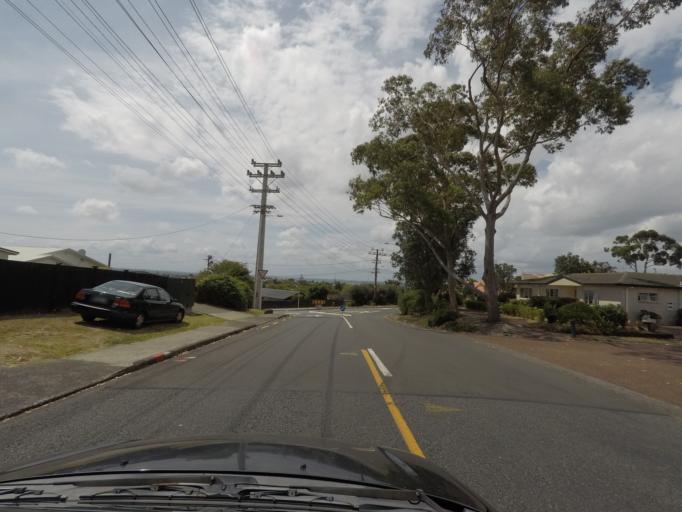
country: NZ
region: Auckland
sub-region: Auckland
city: Waitakere
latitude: -36.8983
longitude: 174.6432
